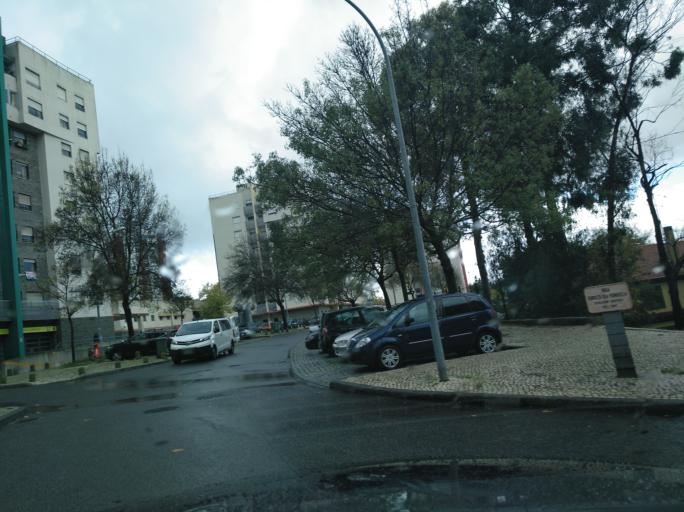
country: PT
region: Lisbon
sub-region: Loures
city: Moscavide
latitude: 38.7613
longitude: -9.1090
